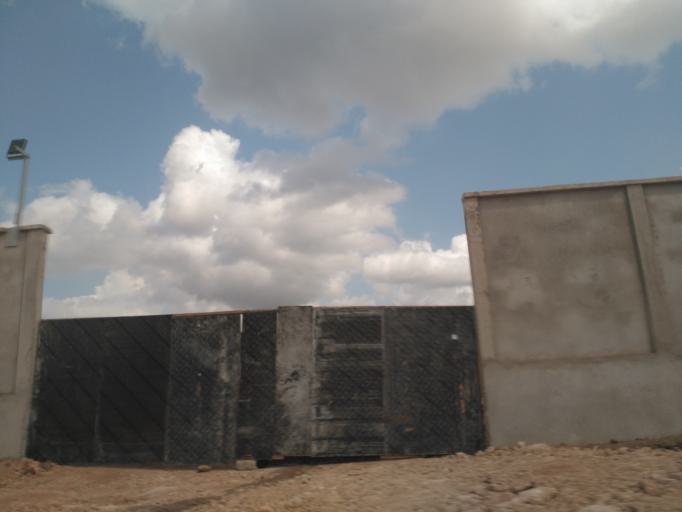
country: TZ
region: Dar es Salaam
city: Dar es Salaam
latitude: -6.8453
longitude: 39.3178
